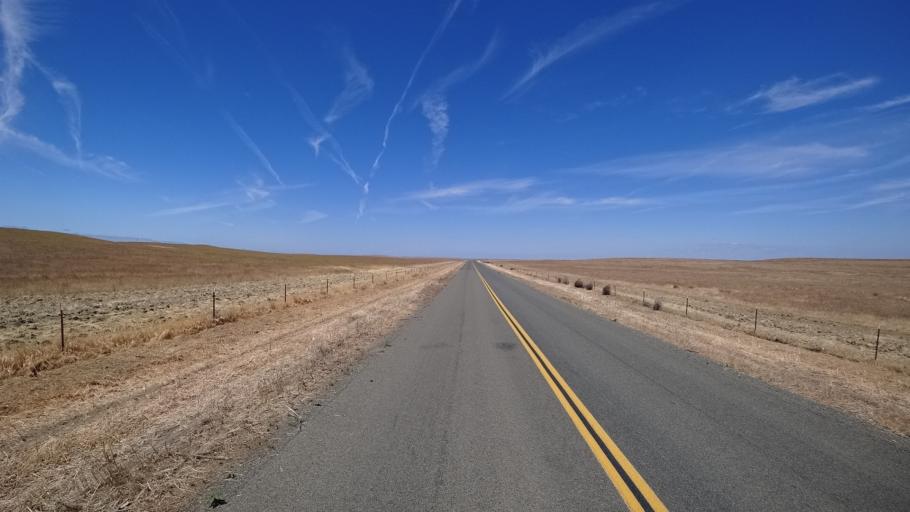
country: US
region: California
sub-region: Kings County
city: Kettleman City
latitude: 35.8142
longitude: -119.9023
